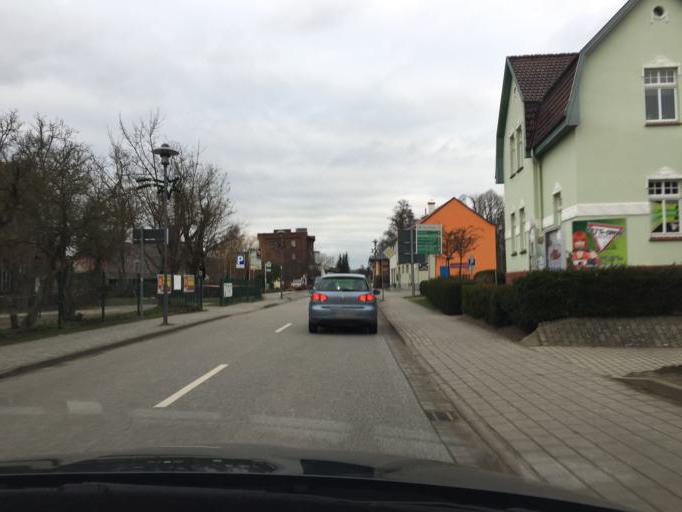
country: DE
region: Brandenburg
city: Burg
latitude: 51.8360
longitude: 14.1486
